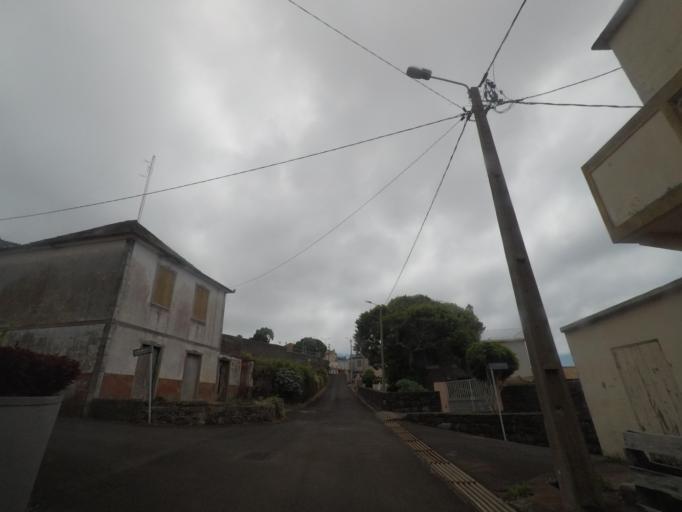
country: PT
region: Madeira
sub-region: Porto Moniz
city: Porto Moniz
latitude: 32.8603
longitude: -17.1892
